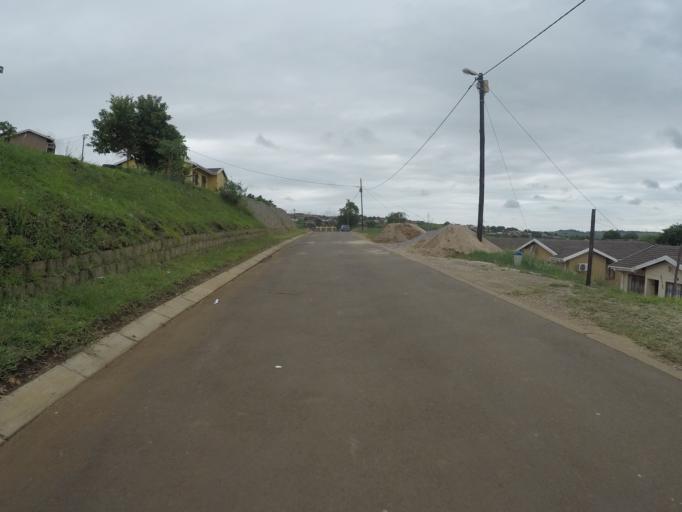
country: ZA
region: KwaZulu-Natal
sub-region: uThungulu District Municipality
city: Empangeni
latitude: -28.7713
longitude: 31.8714
